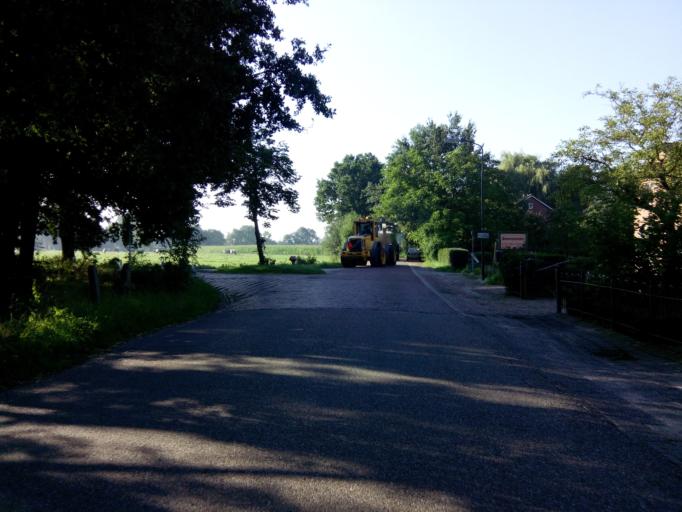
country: NL
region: Utrecht
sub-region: Gemeente Woudenberg
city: Woudenberg
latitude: 52.0736
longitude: 5.4501
